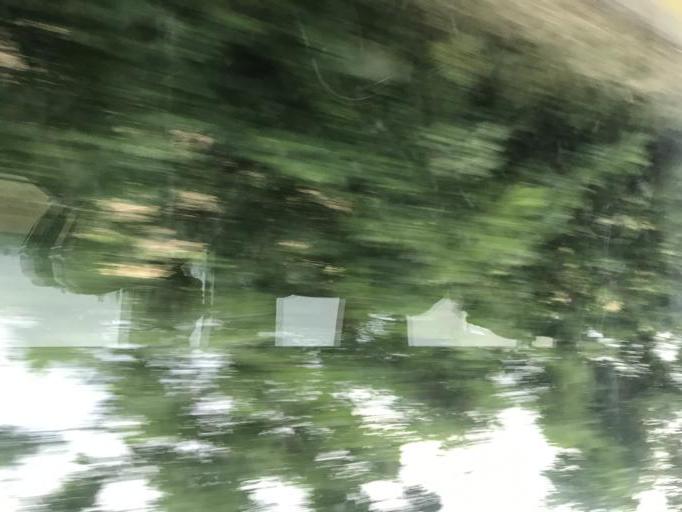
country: GR
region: East Macedonia and Thrace
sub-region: Nomos Rodopis
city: Aratos
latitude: 41.0799
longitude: 25.5612
